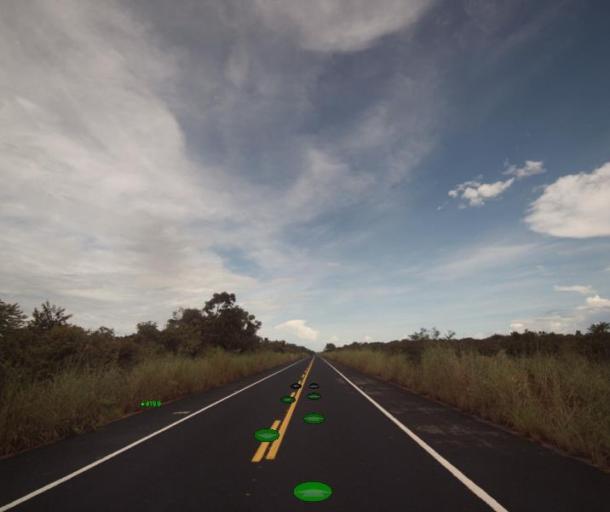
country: BR
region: Goias
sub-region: Sao Miguel Do Araguaia
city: Sao Miguel do Araguaia
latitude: -13.2532
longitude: -50.5264
